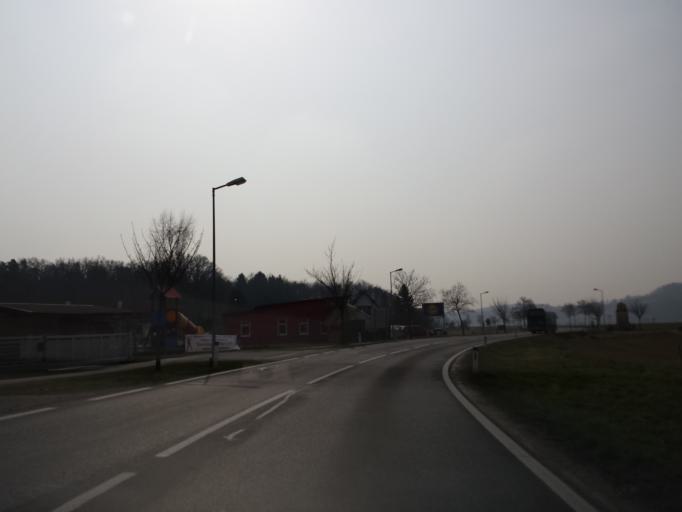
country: AT
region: Styria
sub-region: Politischer Bezirk Hartberg-Fuerstenfeld
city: Fuerstenfeld
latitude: 47.0318
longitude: 16.0883
